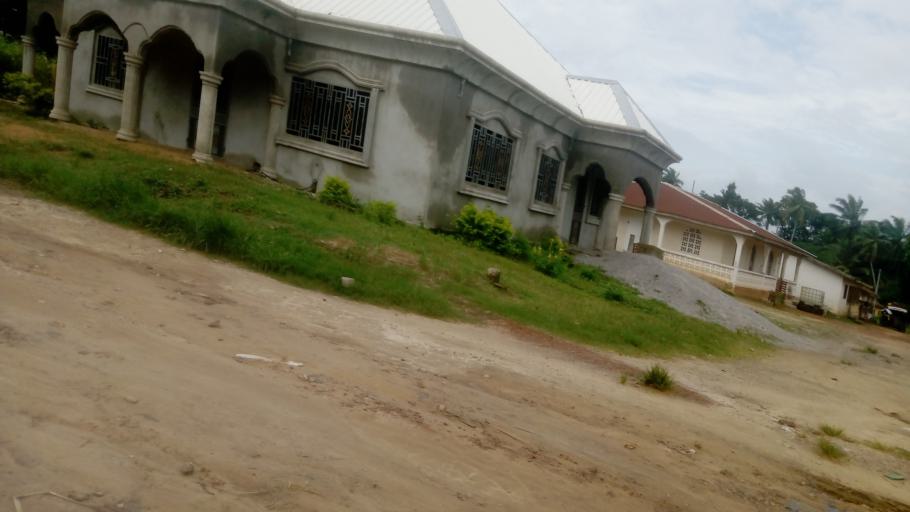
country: SL
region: Northern Province
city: Lunsar
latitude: 8.6876
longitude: -12.5390
